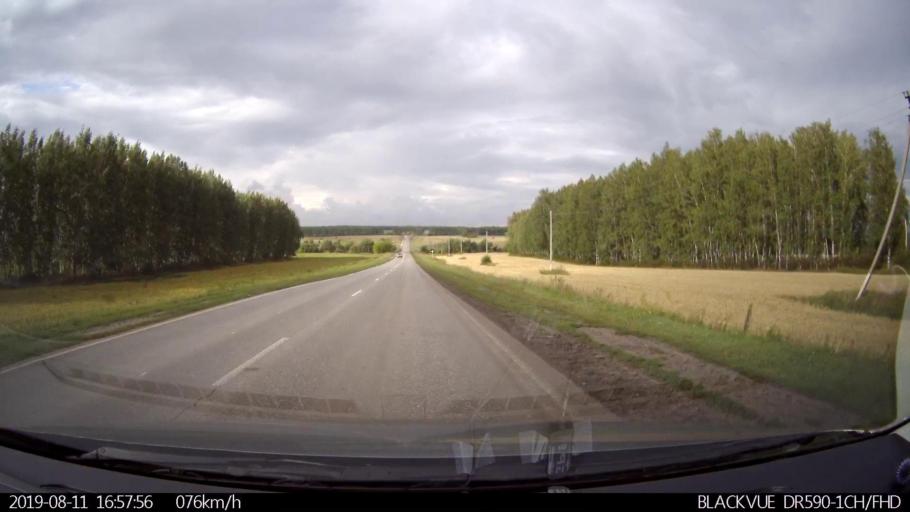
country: RU
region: Ulyanovsk
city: Mayna
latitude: 54.3031
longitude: 47.6548
